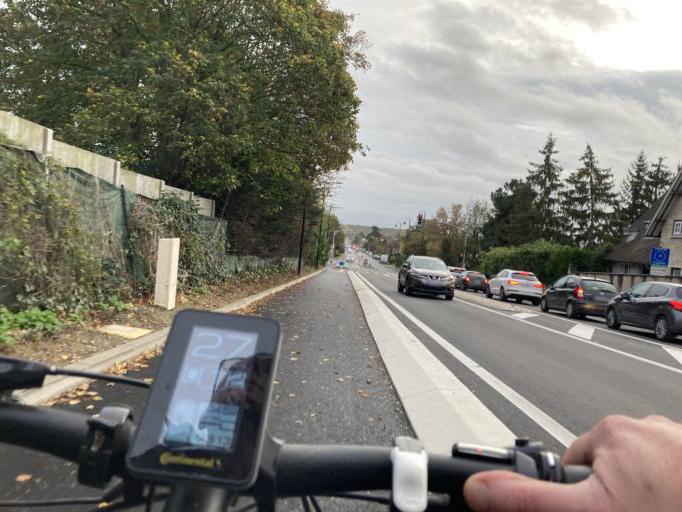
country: FR
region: Picardie
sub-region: Departement de l'Oise
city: Lamorlaye
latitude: 49.1605
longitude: 2.4475
